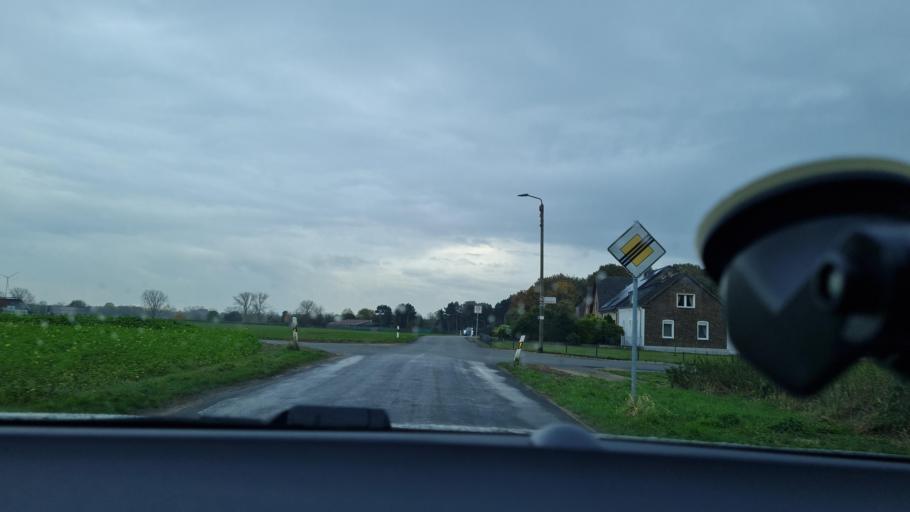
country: DE
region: North Rhine-Westphalia
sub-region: Regierungsbezirk Dusseldorf
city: Voerde
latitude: 51.6036
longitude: 6.6252
